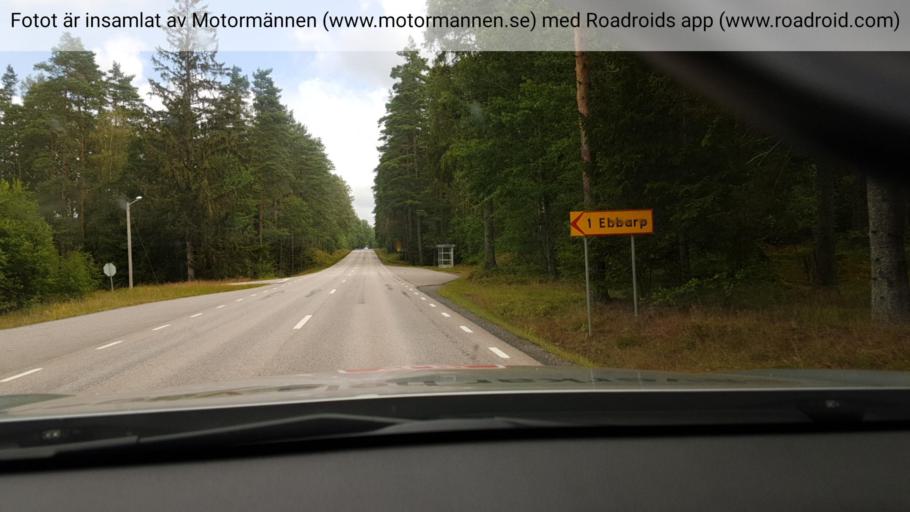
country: SE
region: Vaestra Goetaland
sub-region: Svenljunga Kommun
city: Svenljunga
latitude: 57.4886
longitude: 13.0616
